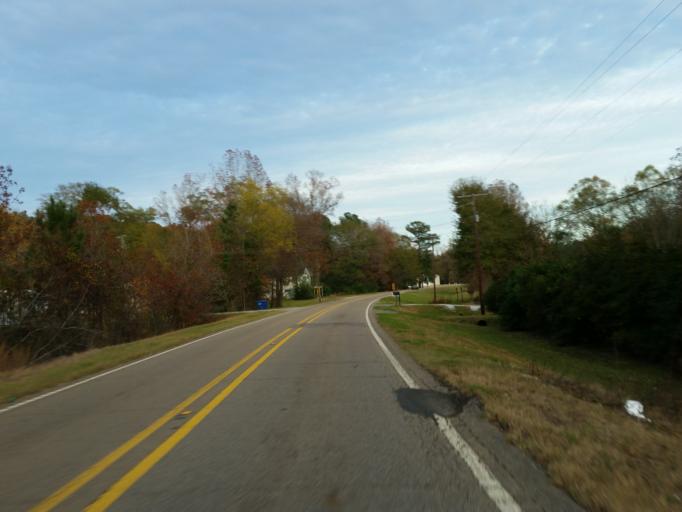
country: US
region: Mississippi
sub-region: Lauderdale County
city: Marion
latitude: 32.4113
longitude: -88.5586
